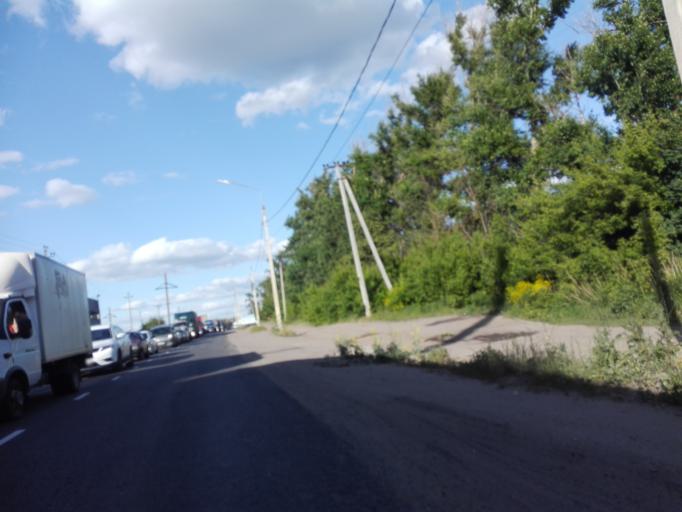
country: RU
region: Orjol
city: Orel
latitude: 52.9383
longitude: 36.0638
